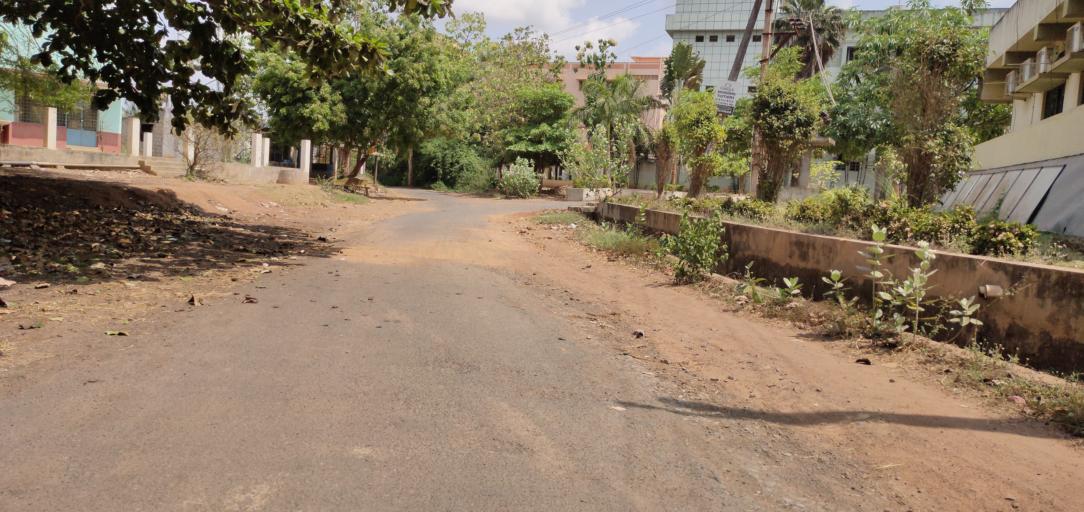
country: IN
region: Andhra Pradesh
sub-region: West Godavari
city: Tadepallegudem
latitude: 16.8589
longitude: 81.4939
